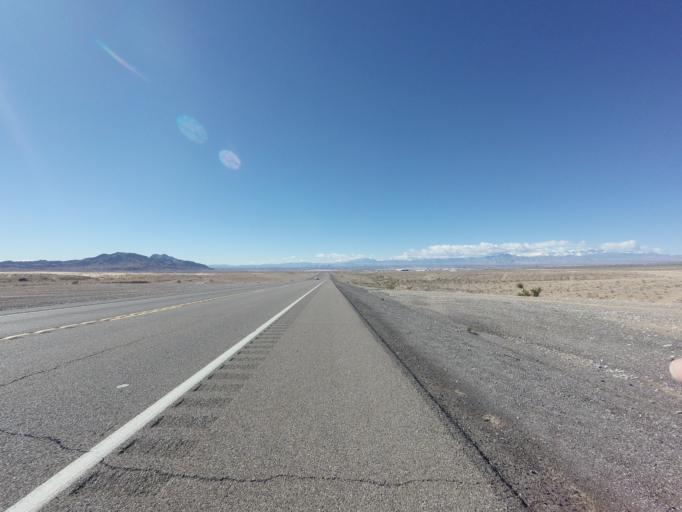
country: US
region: Nevada
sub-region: Clark County
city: Nellis Air Force Base
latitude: 36.2999
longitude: -114.9589
